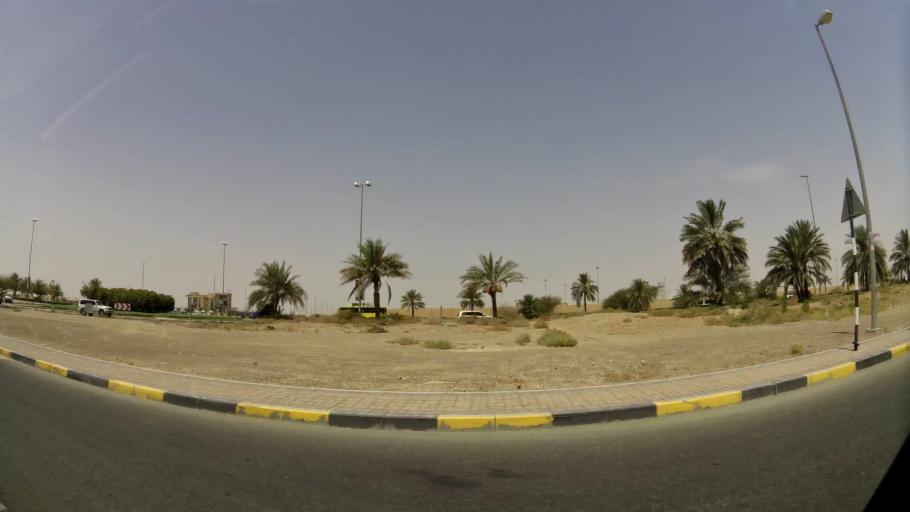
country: AE
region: Abu Dhabi
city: Al Ain
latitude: 24.1960
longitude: 55.7298
